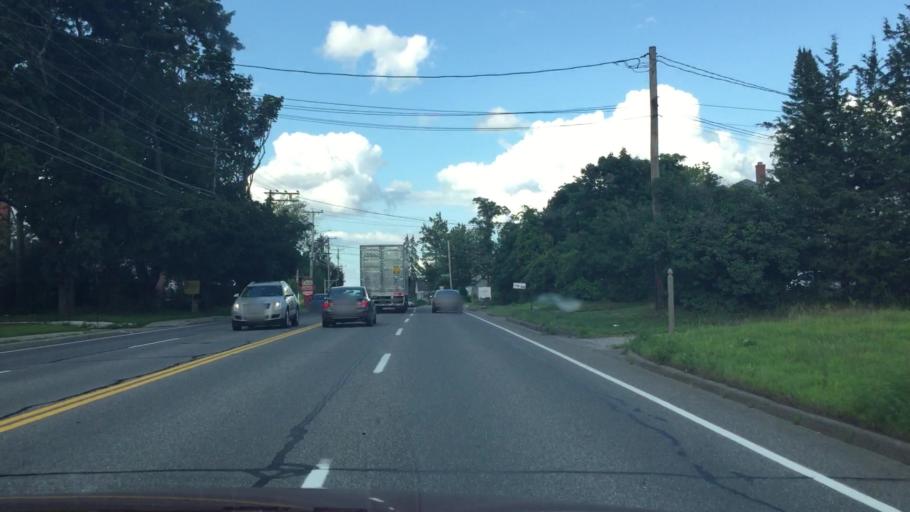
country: US
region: Maine
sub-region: Cumberland County
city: West Scarborough
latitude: 43.5654
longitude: -70.3940
